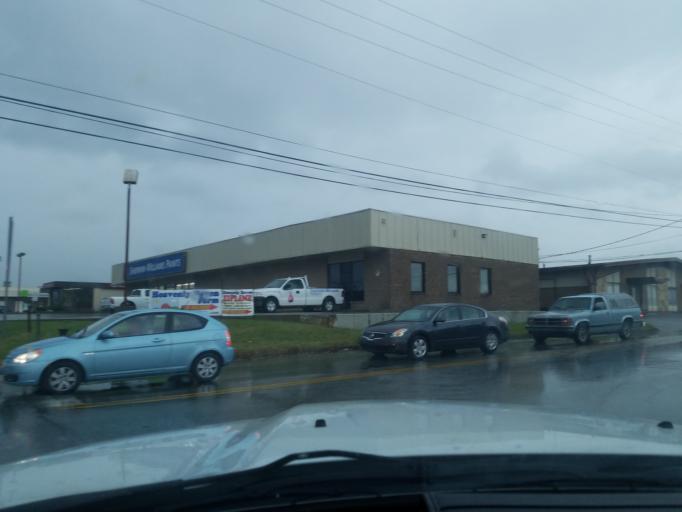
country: US
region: Kentucky
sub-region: Taylor County
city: Campbellsville
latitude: 37.3511
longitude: -85.3320
